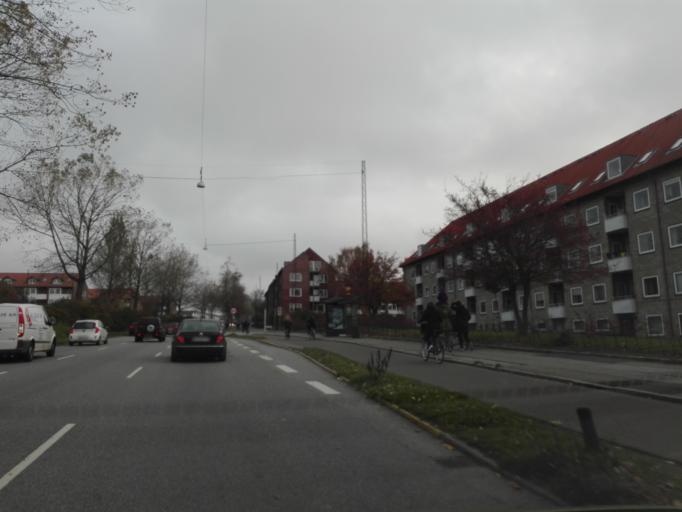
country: DK
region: Central Jutland
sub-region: Arhus Kommune
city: Arhus
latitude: 56.1653
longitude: 10.1877
